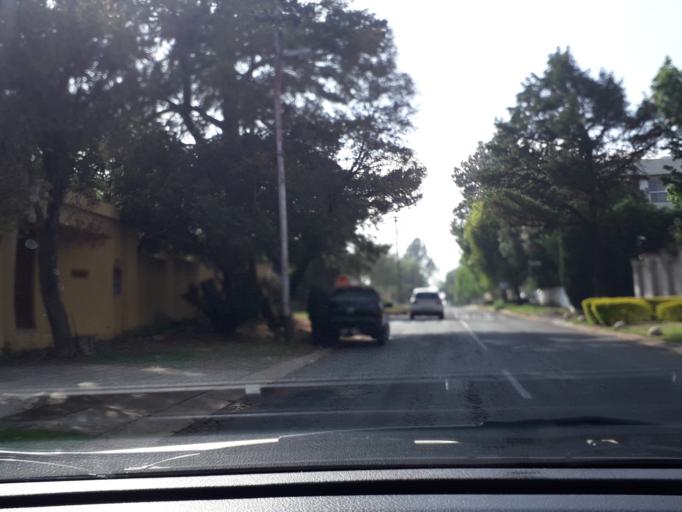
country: ZA
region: Gauteng
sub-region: City of Johannesburg Metropolitan Municipality
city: Johannesburg
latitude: -26.0941
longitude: 28.0345
